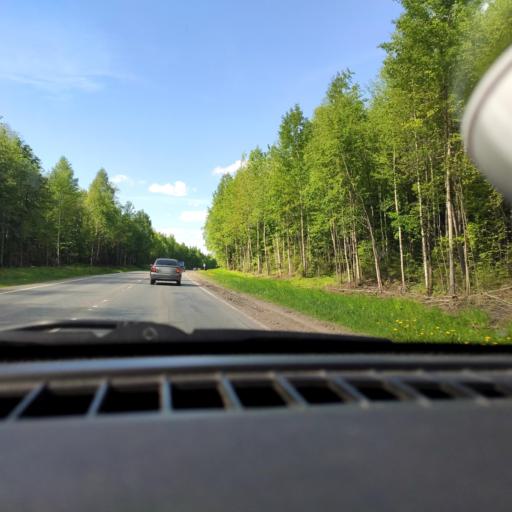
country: RU
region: Perm
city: Perm
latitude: 58.2219
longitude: 56.1663
